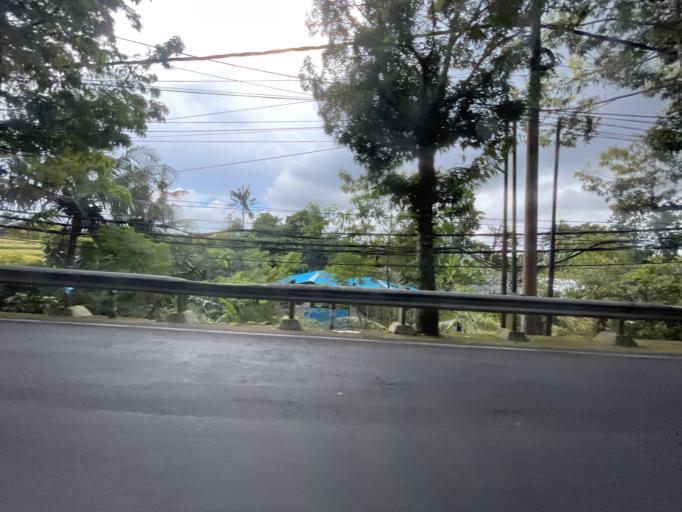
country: ID
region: Bali
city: Banjar Sedang
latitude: -8.5656
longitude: 115.2835
